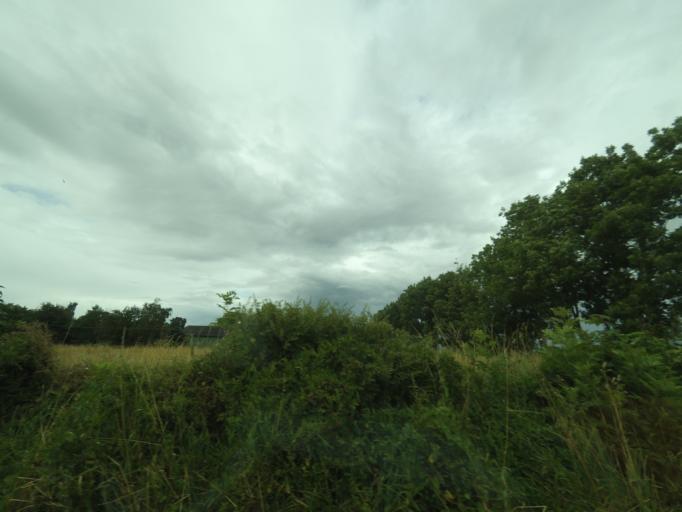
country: DK
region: South Denmark
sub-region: Nordfyns Kommune
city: Otterup
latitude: 55.4869
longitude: 10.3476
